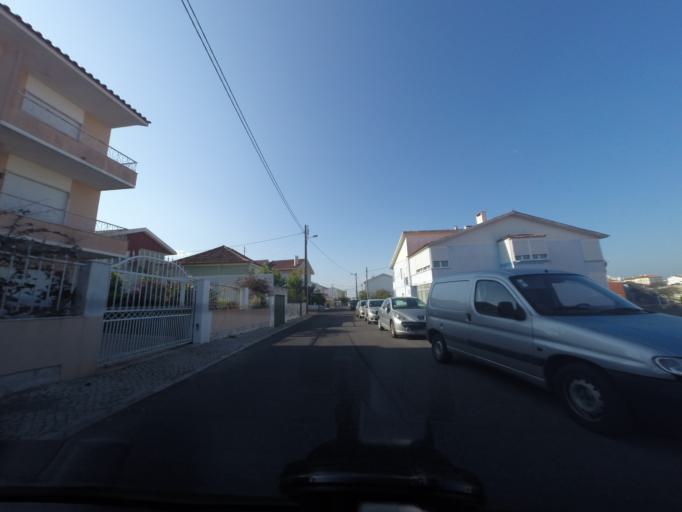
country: PT
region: Lisbon
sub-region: Cascais
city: Sao Domingos de Rana
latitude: 38.7064
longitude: -9.3429
